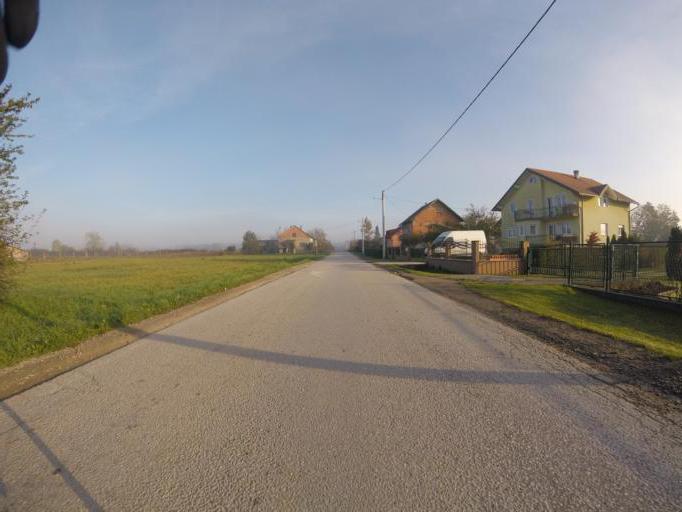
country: HR
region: Zagrebacka
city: Kuce
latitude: 45.7057
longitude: 16.1188
